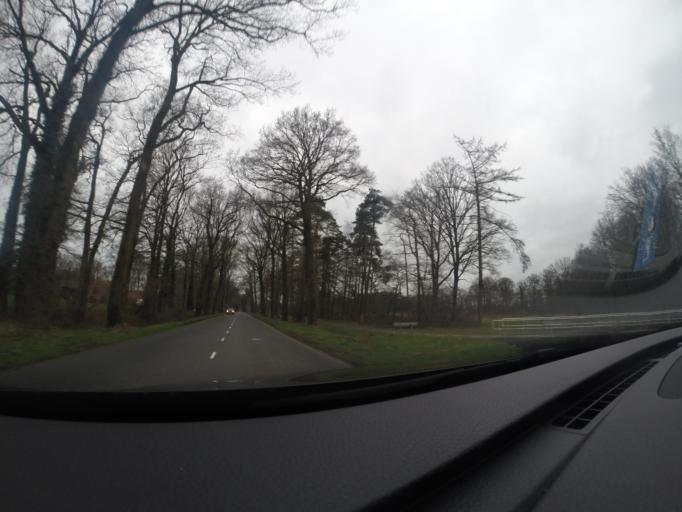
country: NL
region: Gelderland
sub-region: Berkelland
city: Eibergen
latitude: 52.0943
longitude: 6.6844
